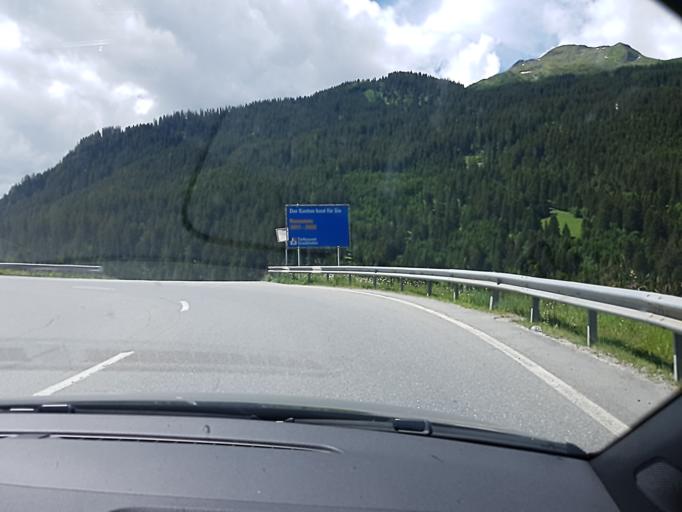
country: CH
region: Grisons
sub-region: Albula District
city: Tiefencastel
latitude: 46.5749
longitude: 9.6226
